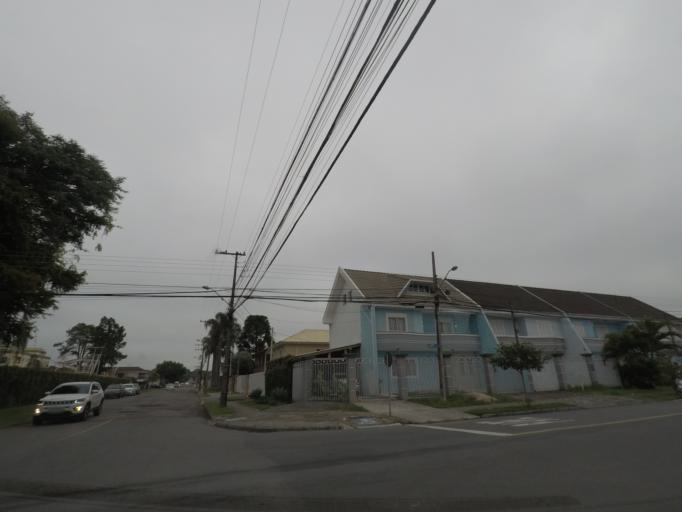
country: BR
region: Parana
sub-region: Curitiba
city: Curitiba
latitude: -25.4796
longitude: -49.2508
